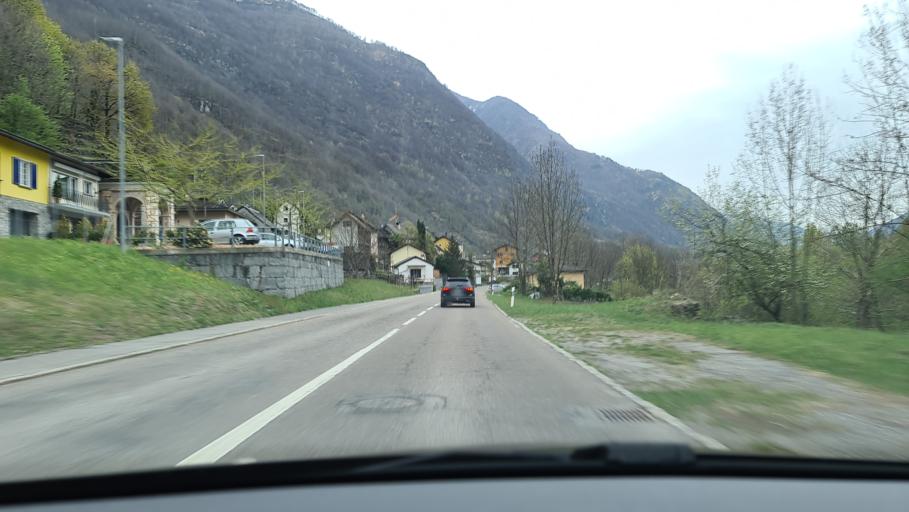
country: CH
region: Ticino
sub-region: Vallemaggia District
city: Cevio
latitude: 46.2885
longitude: 8.6582
